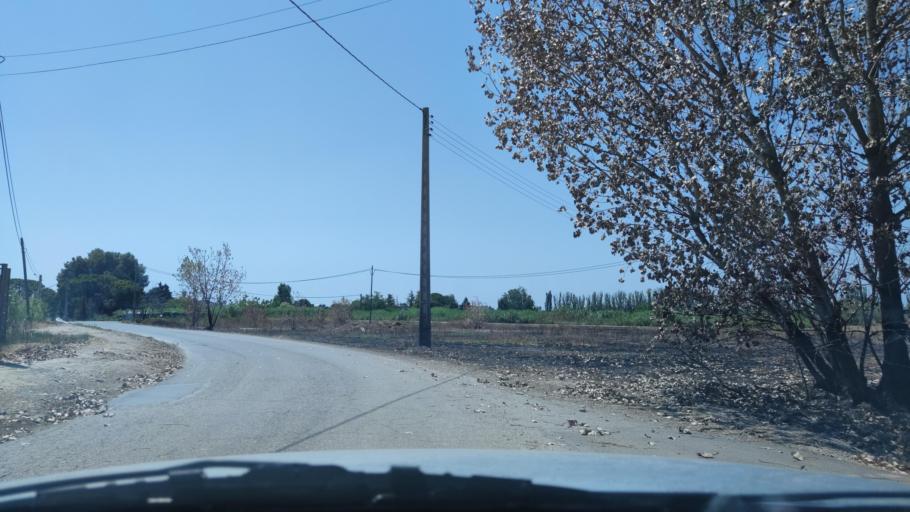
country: ES
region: Catalonia
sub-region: Provincia de Lleida
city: Lleida
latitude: 41.6359
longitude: 0.5974
